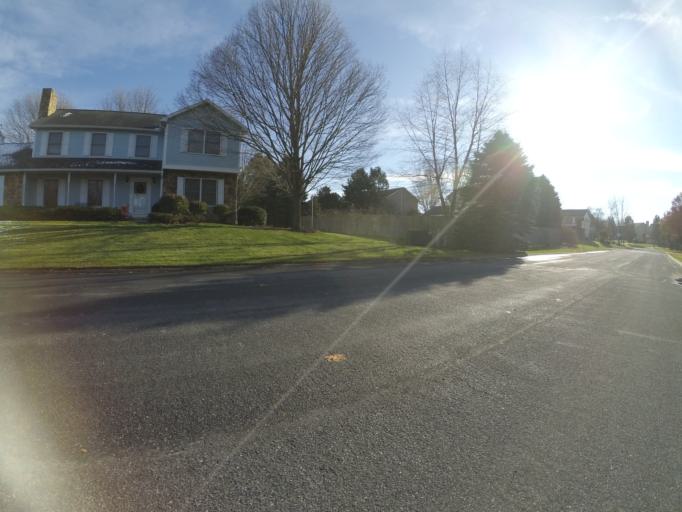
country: US
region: Pennsylvania
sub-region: Centre County
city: Pine Grove Mills
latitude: 40.7702
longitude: -77.8911
